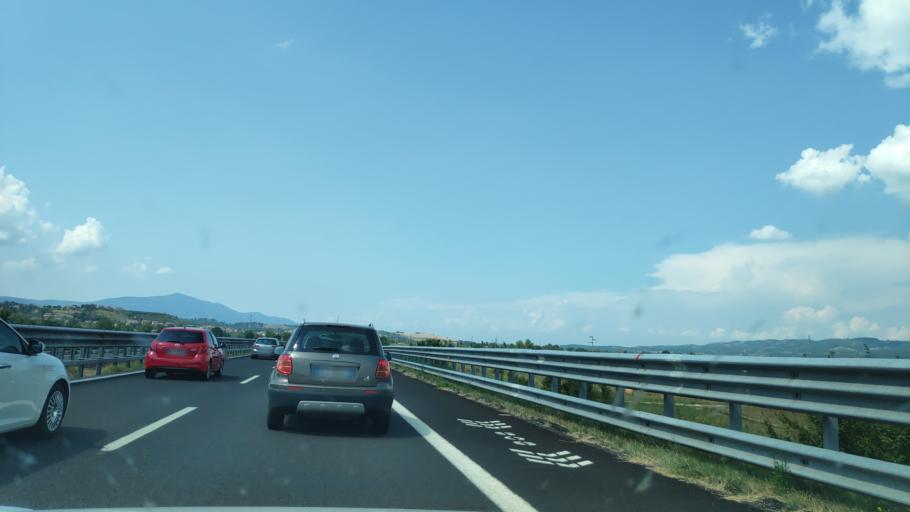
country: IT
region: Umbria
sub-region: Provincia di Terni
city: Fabro Scalo
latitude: 42.8626
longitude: 12.0355
